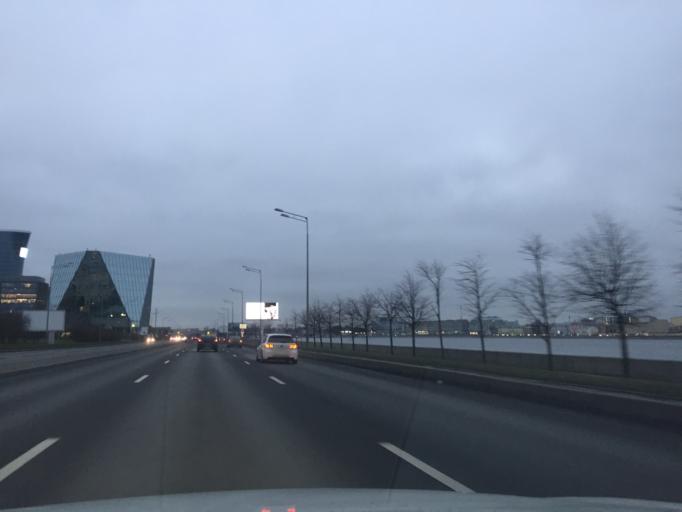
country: RU
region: St.-Petersburg
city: Centralniy
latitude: 59.9369
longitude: 30.4028
